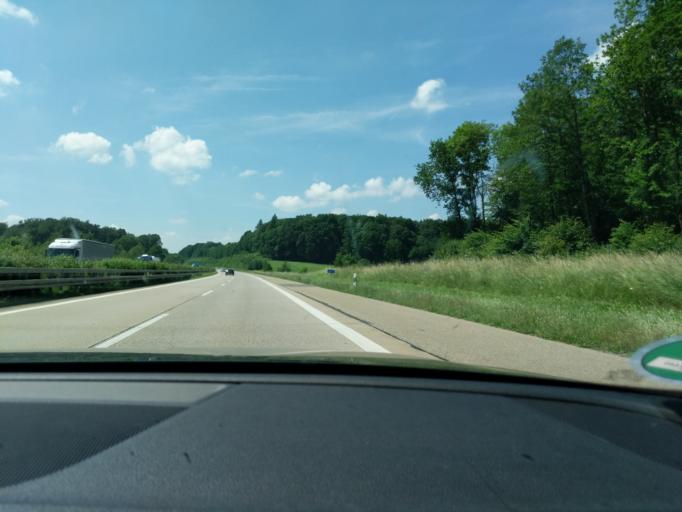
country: DE
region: Baden-Wuerttemberg
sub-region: Regierungsbezirk Stuttgart
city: Widdern
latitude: 49.3604
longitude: 9.4217
